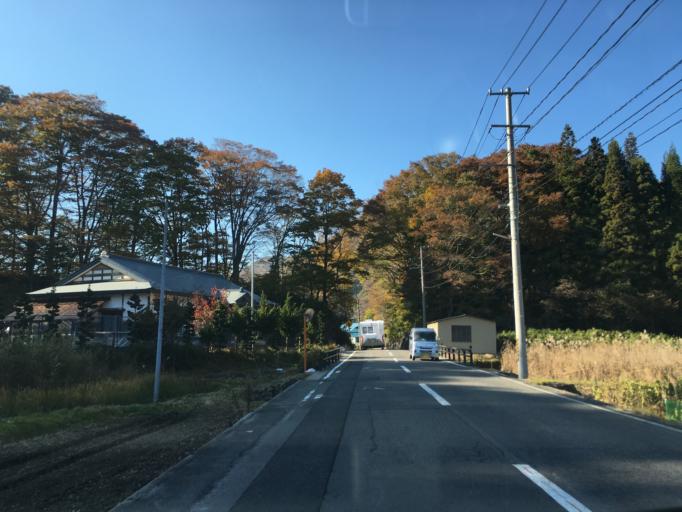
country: JP
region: Fukushima
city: Inawashiro
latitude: 37.2792
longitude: 140.0089
